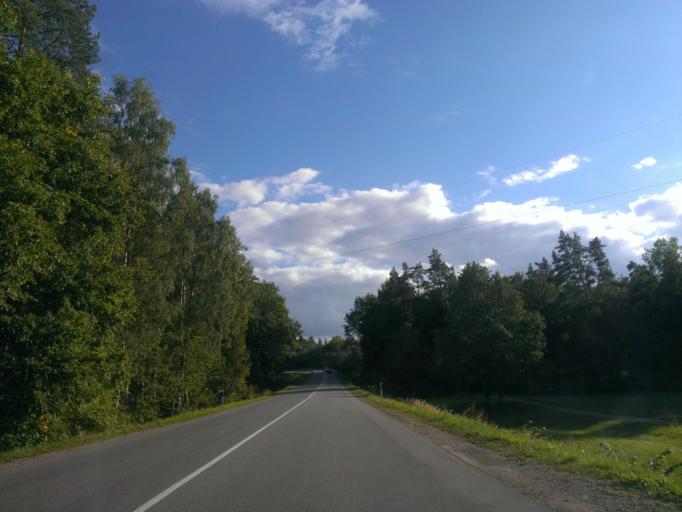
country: LV
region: Sigulda
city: Sigulda
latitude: 57.1686
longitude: 24.8381
